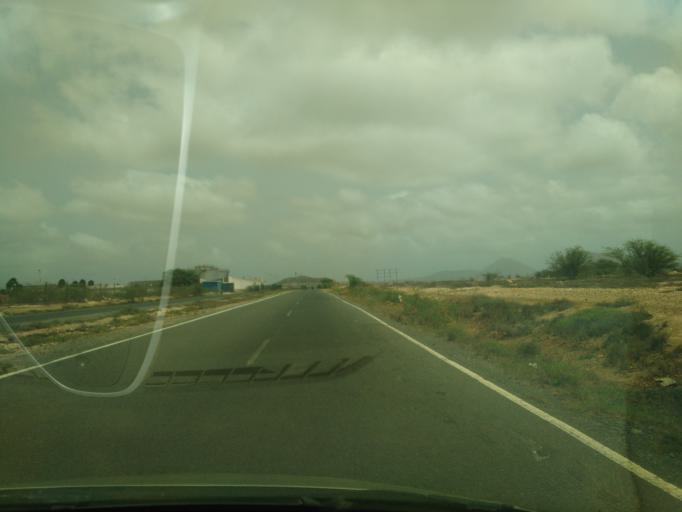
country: CV
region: Sal
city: Espargos
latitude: 16.7295
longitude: -22.9417
